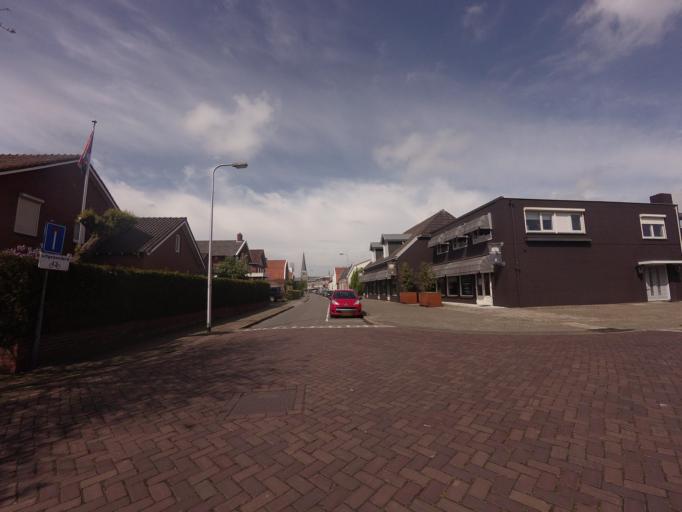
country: NL
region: Overijssel
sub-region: Gemeente Haaksbergen
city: Haaksbergen
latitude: 52.1517
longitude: 6.7410
